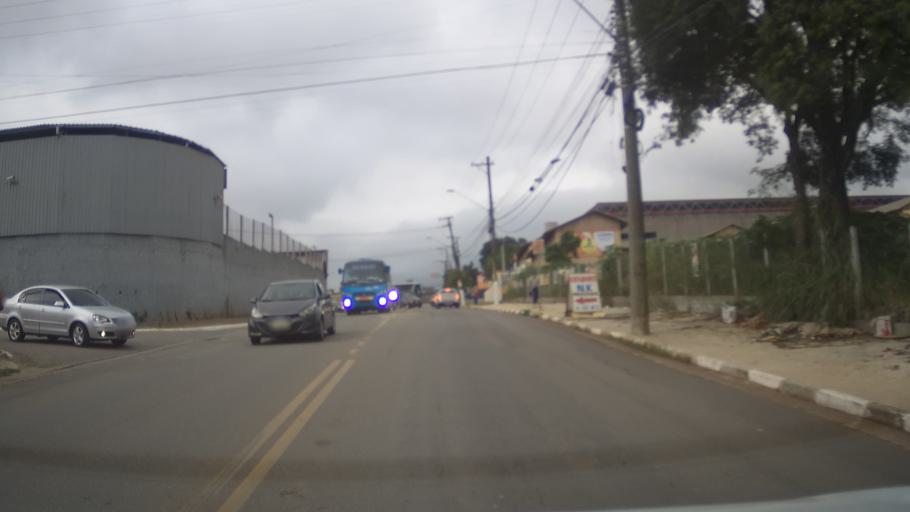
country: BR
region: Sao Paulo
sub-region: Aruja
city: Aruja
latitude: -23.4072
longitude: -46.3878
